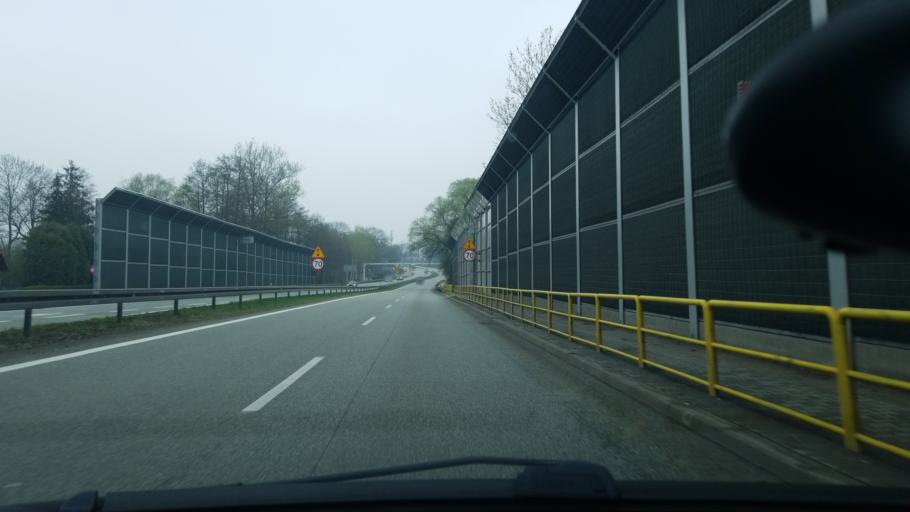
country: PL
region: Silesian Voivodeship
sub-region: Powiat pszczynski
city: Pawlowice
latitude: 49.9961
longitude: 18.7114
